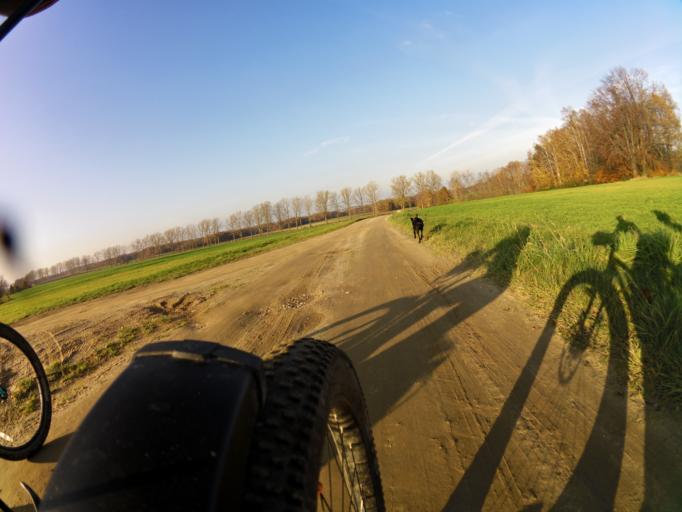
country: PL
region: Pomeranian Voivodeship
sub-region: Powiat pucki
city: Krokowa
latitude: 54.7331
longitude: 18.1972
